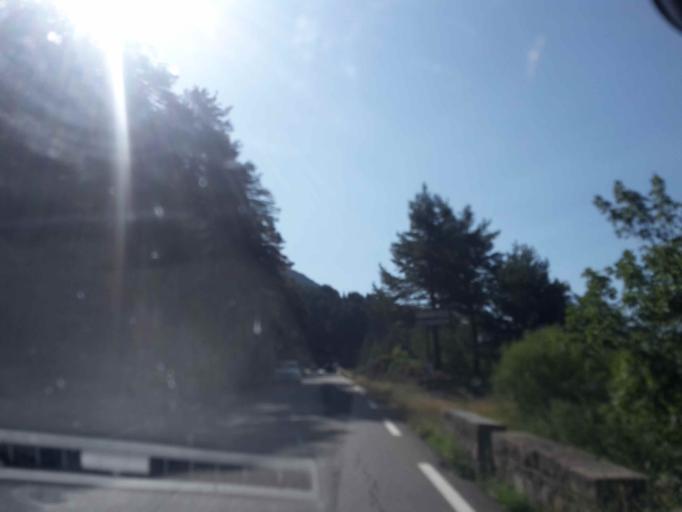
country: FR
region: Provence-Alpes-Cote d'Azur
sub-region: Departement des Hautes-Alpes
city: Guillestre
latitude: 44.6303
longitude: 6.6779
